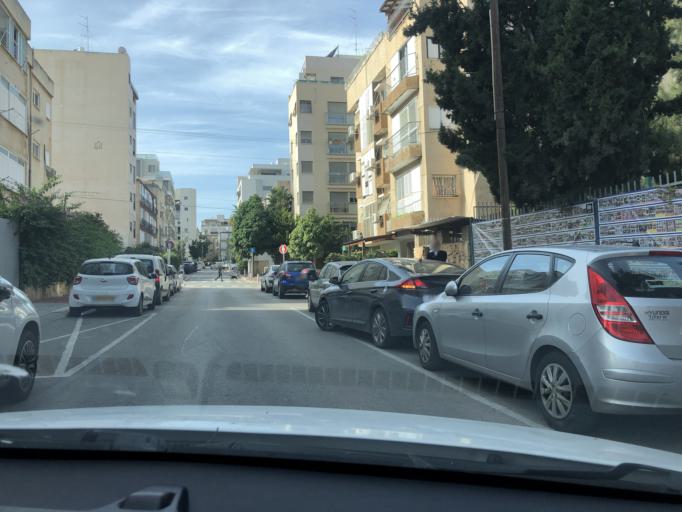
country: IL
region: Tel Aviv
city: Bene Beraq
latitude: 32.0689
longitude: 34.8278
